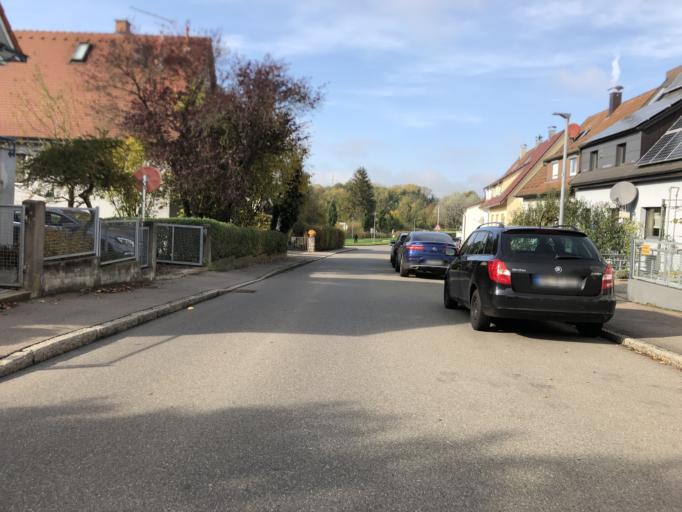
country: DE
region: Baden-Wuerttemberg
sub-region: Regierungsbezirk Stuttgart
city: Sindelfingen
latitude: 48.7143
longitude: 8.9928
